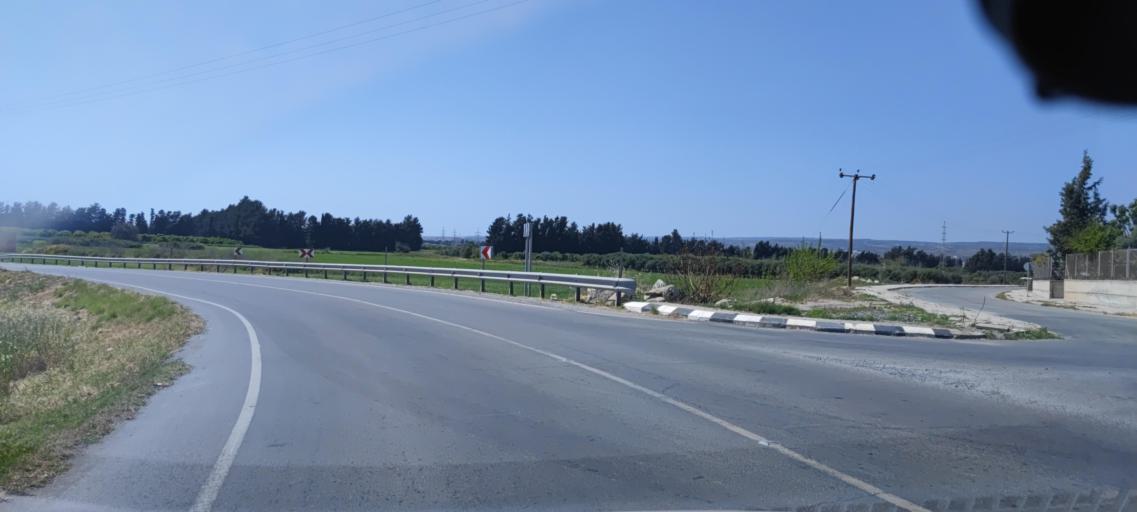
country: CY
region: Larnaka
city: Kolossi
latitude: 34.6563
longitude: 32.9491
